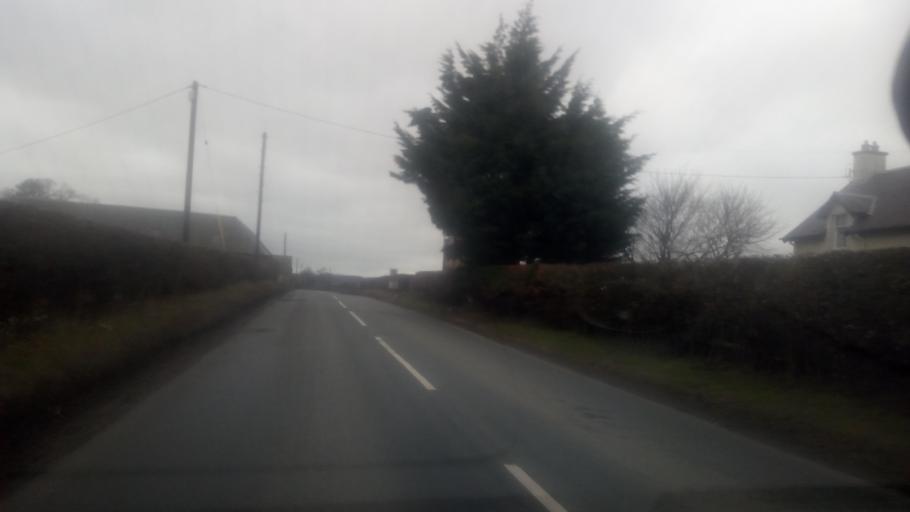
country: GB
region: Scotland
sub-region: The Scottish Borders
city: Kelso
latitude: 55.5845
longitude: -2.4923
